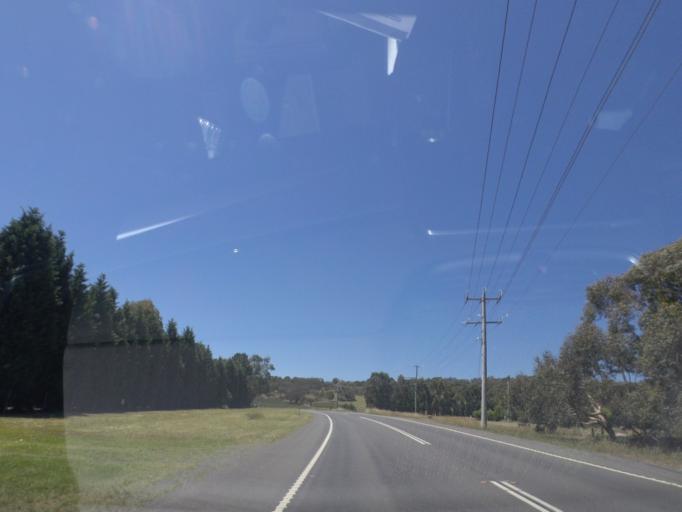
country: AU
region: Victoria
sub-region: Whittlesea
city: Whittlesea
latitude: -37.4304
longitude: 145.0201
